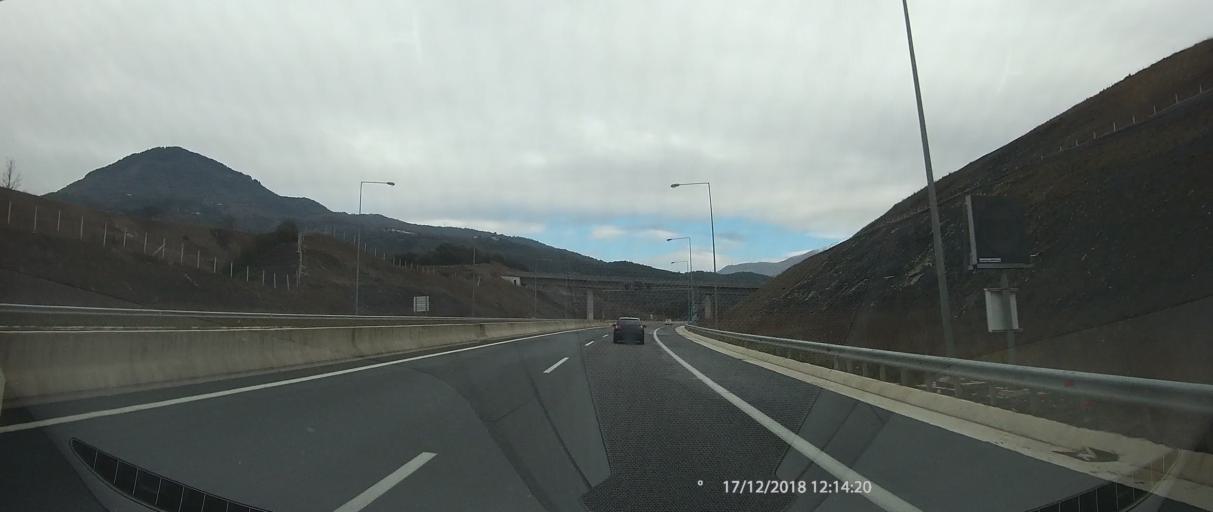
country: GR
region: Epirus
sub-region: Nomos Ioanninon
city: Katsikas
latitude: 39.7176
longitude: 20.9943
